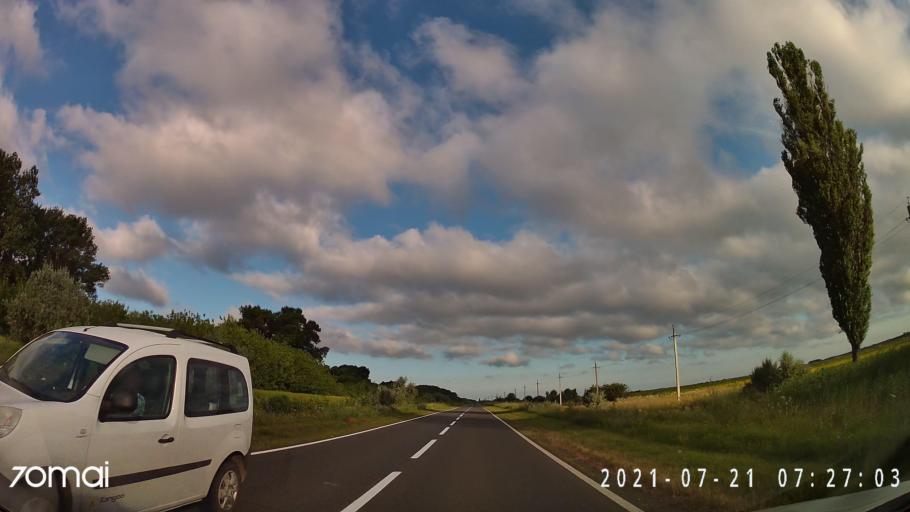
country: RO
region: Tulcea
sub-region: Oras Isaccea
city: Isaccea
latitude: 45.3010
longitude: 28.4259
